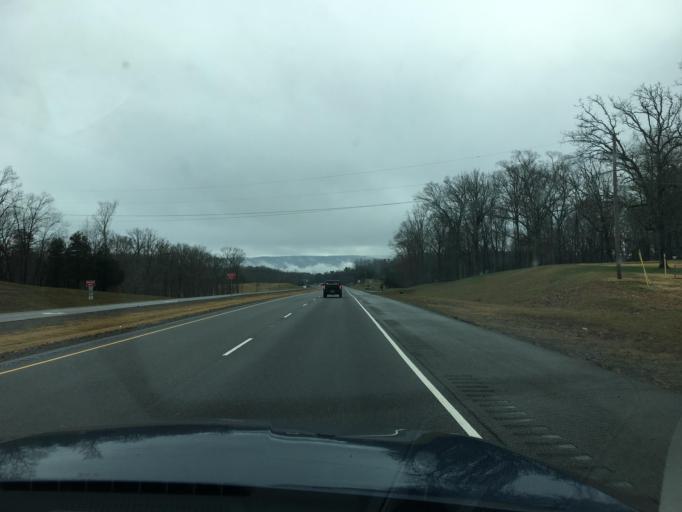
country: US
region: Tennessee
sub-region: McMinn County
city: Etowah
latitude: 35.3514
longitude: -84.5505
